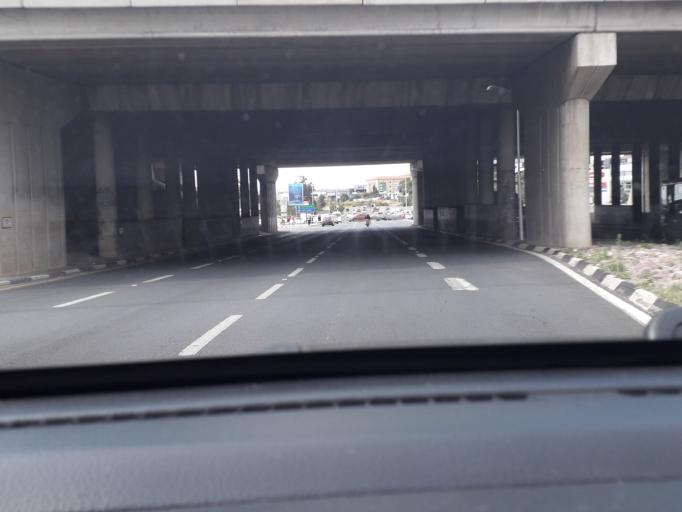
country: ZA
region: Gauteng
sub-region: City of Johannesburg Metropolitan Municipality
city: Midrand
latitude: -26.0388
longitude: 28.0607
